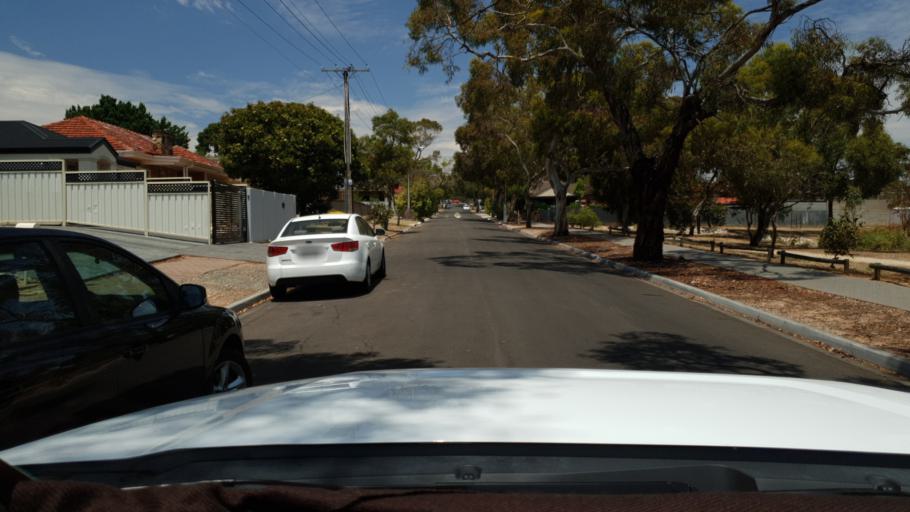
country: AU
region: South Australia
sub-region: Marion
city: Clovelly Park
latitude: -35.0078
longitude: 138.5814
